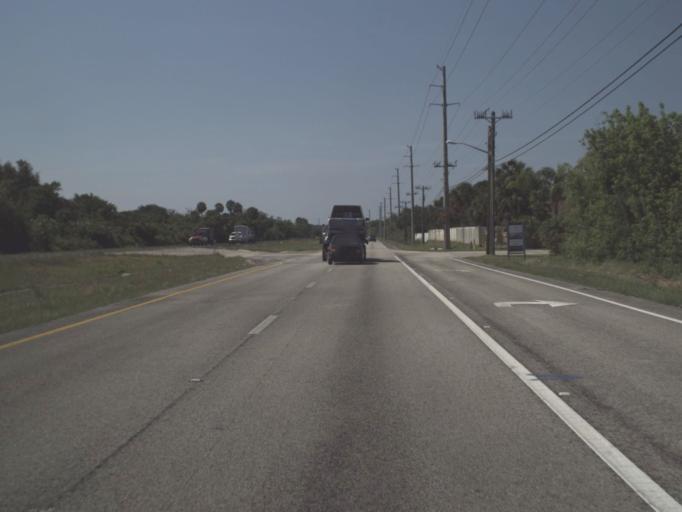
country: US
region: Florida
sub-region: Brevard County
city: South Patrick Shores
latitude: 28.2420
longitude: -80.6780
